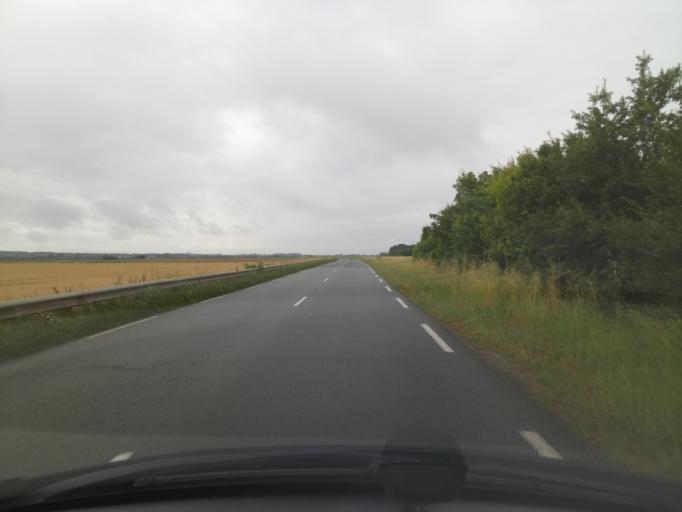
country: FR
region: Poitou-Charentes
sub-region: Departement de la Charente-Maritime
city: Saint-Jean-de-Liversay
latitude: 46.2036
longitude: -0.8730
